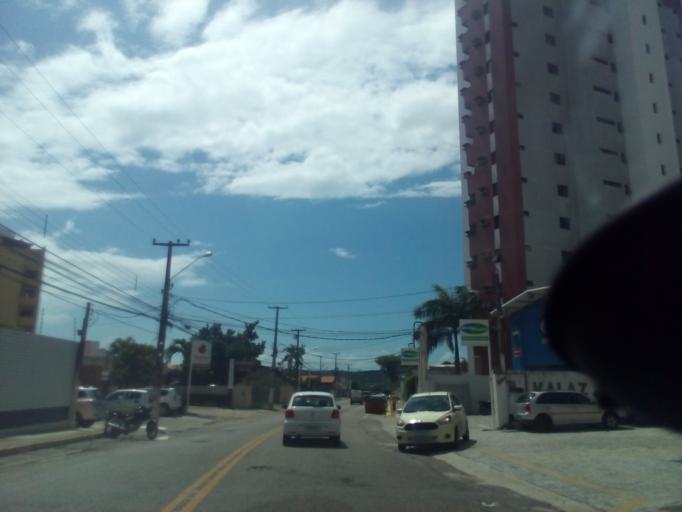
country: BR
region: Rio Grande do Norte
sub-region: Natal
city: Natal
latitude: -5.8388
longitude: -35.2146
